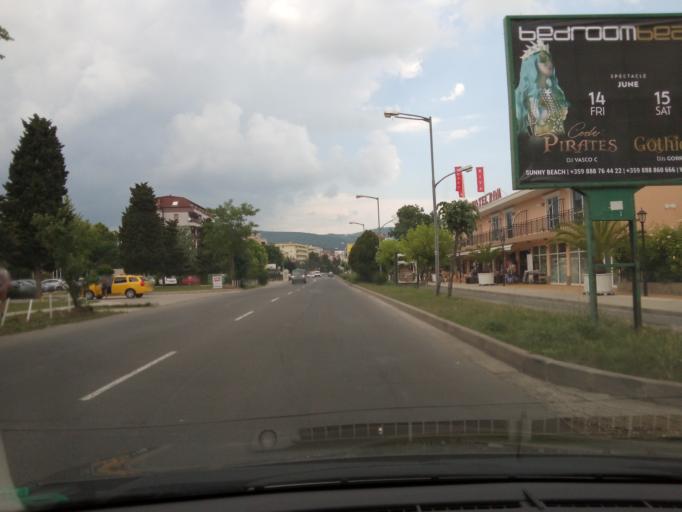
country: BG
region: Burgas
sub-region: Obshtina Nesebur
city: Sveti Vlas
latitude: 42.7027
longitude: 27.7153
